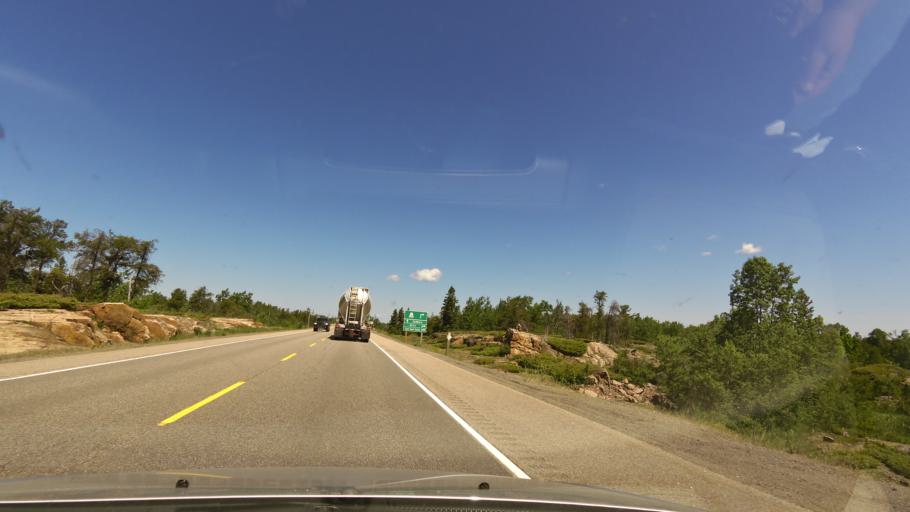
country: CA
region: Ontario
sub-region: Parry Sound District
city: Parry Sound
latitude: 45.7982
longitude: -80.5349
